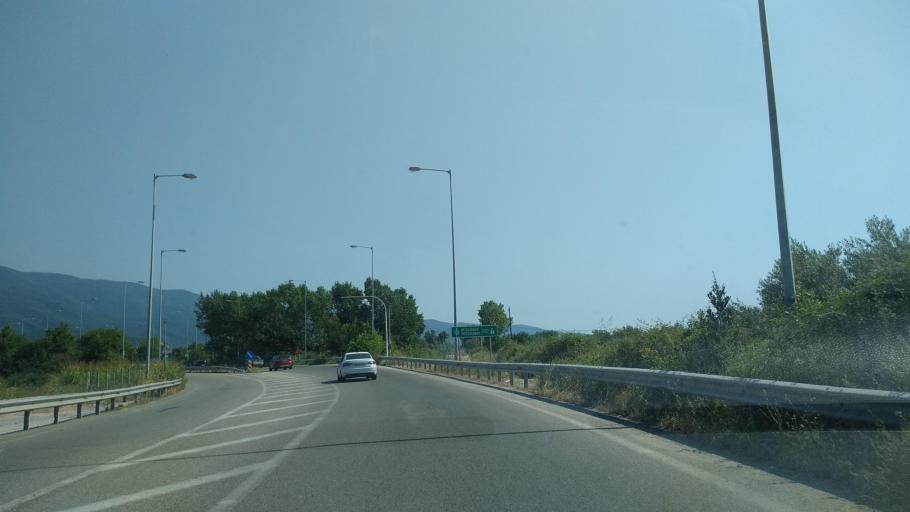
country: GR
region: Central Macedonia
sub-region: Nomos Thessalonikis
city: Nea Vrasna
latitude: 40.7021
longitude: 23.6915
